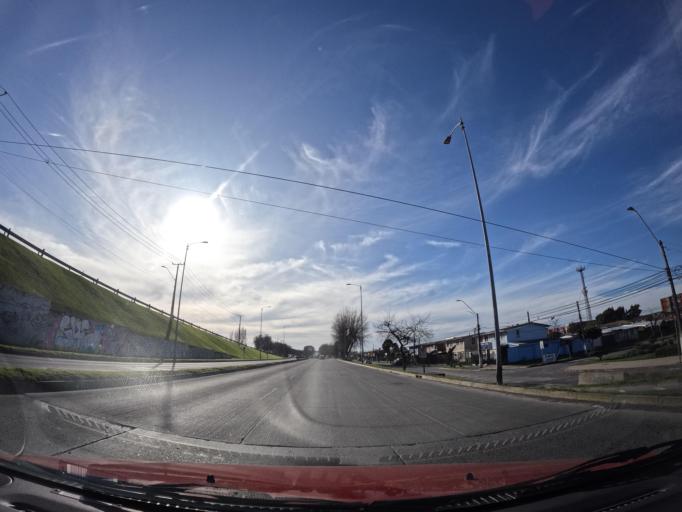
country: CL
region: Biobio
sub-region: Provincia de Concepcion
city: Talcahuano
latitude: -36.7650
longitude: -73.0861
